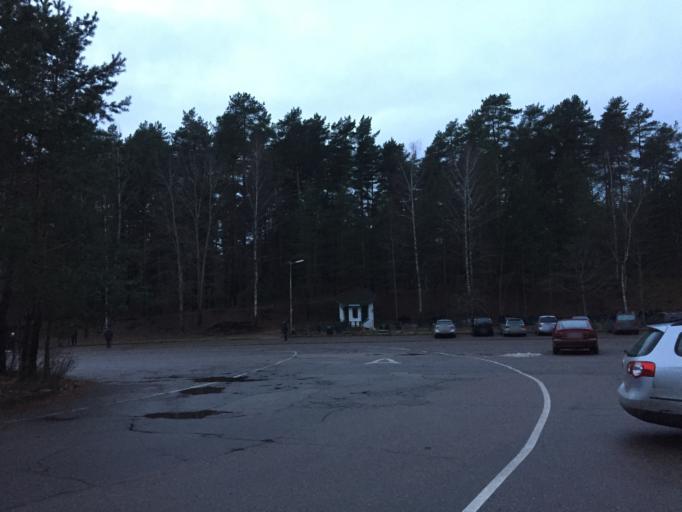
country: LV
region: Riga
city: Jaunciems
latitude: 57.0418
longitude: 24.1894
